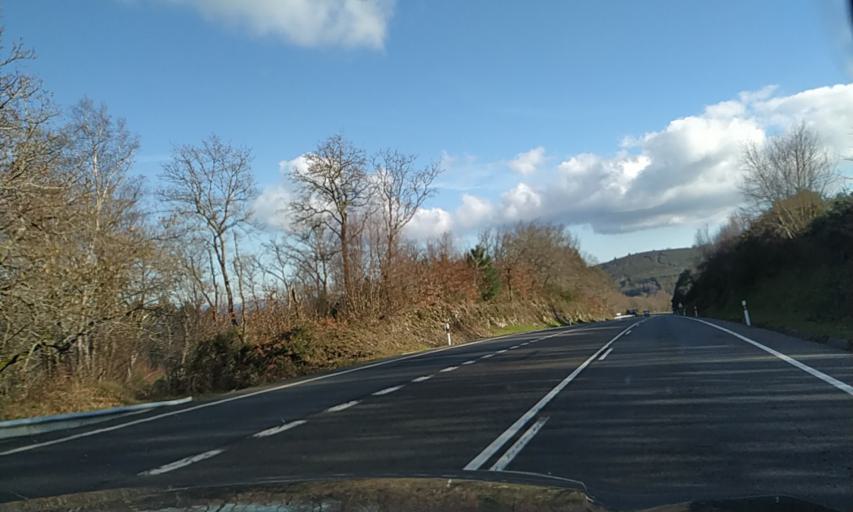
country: ES
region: Galicia
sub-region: Provincia de Pontevedra
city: Silleda
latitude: 42.7036
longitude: -8.3426
